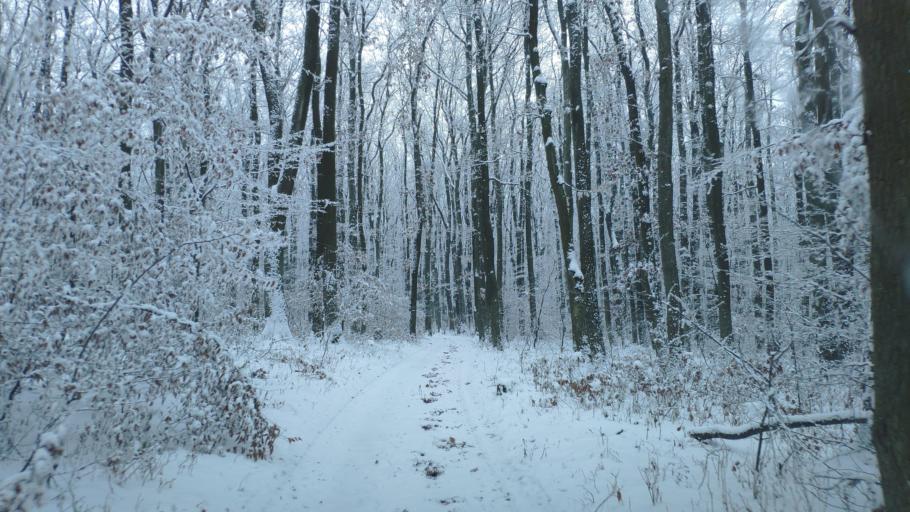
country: SK
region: Kosicky
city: Kosice
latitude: 48.6592
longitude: 21.1829
